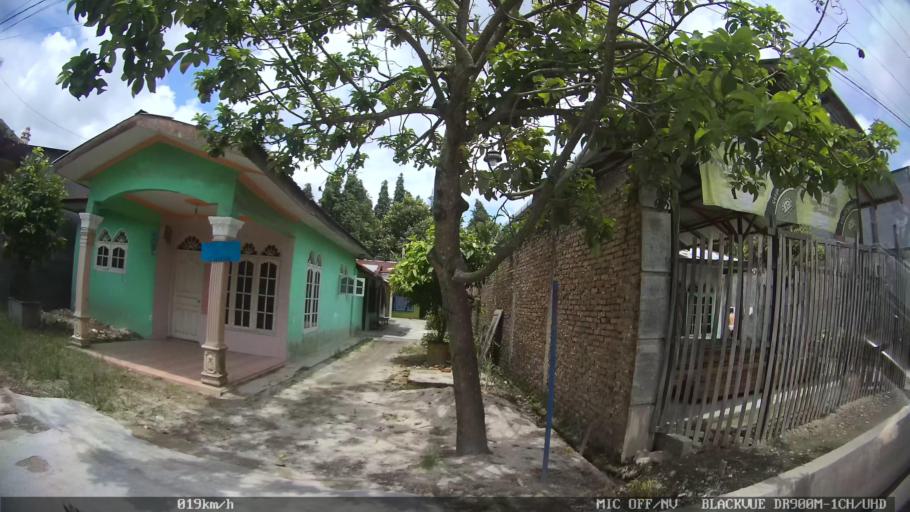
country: ID
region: North Sumatra
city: Medan
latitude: 3.6110
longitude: 98.7480
